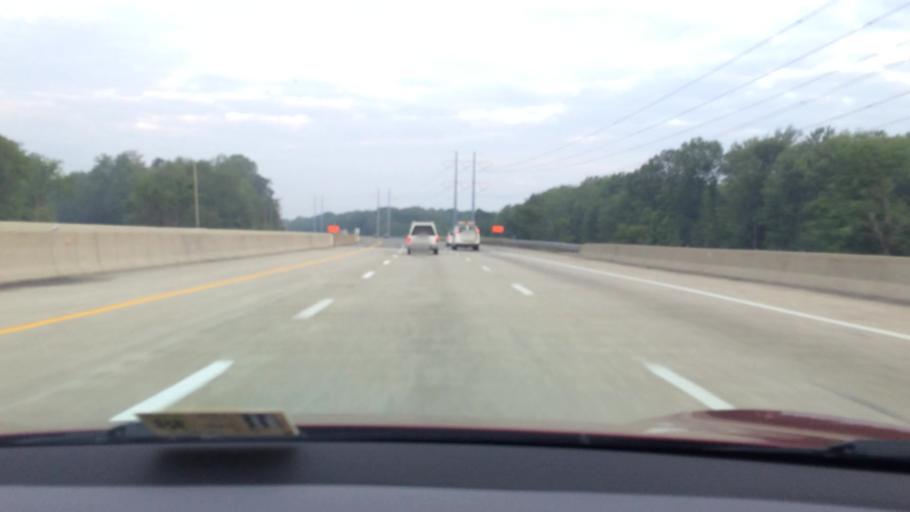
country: US
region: Ohio
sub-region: Cuyahoga County
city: Broadview Heights
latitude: 41.3010
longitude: -81.7005
